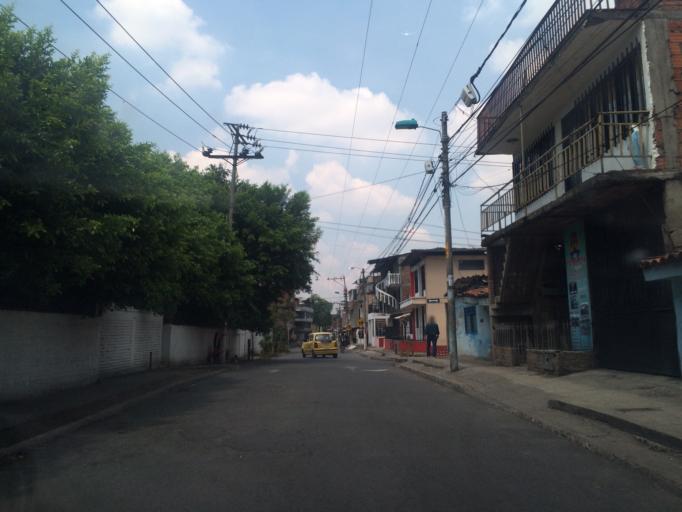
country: CO
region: Valle del Cauca
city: Cali
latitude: 3.4939
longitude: -76.4899
